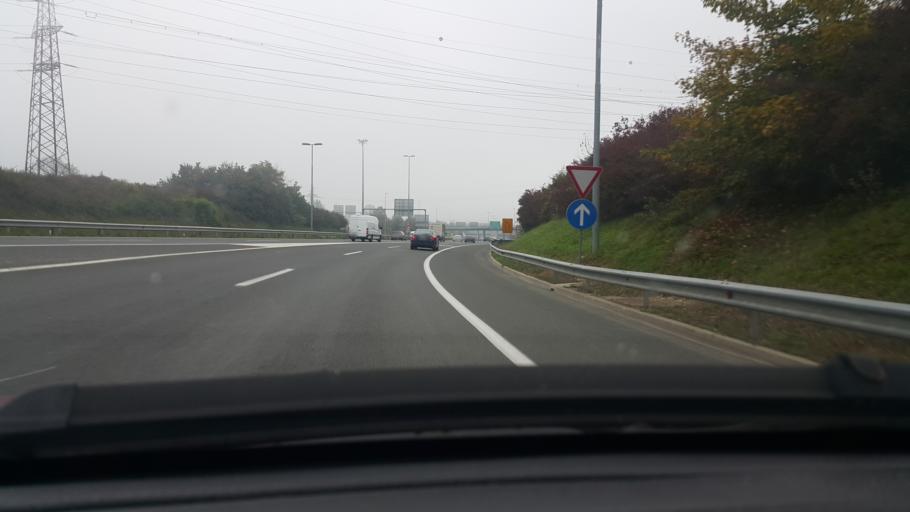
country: SI
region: Dol pri Ljubljani
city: Dol pri Ljubljani
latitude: 46.0655
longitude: 14.5754
